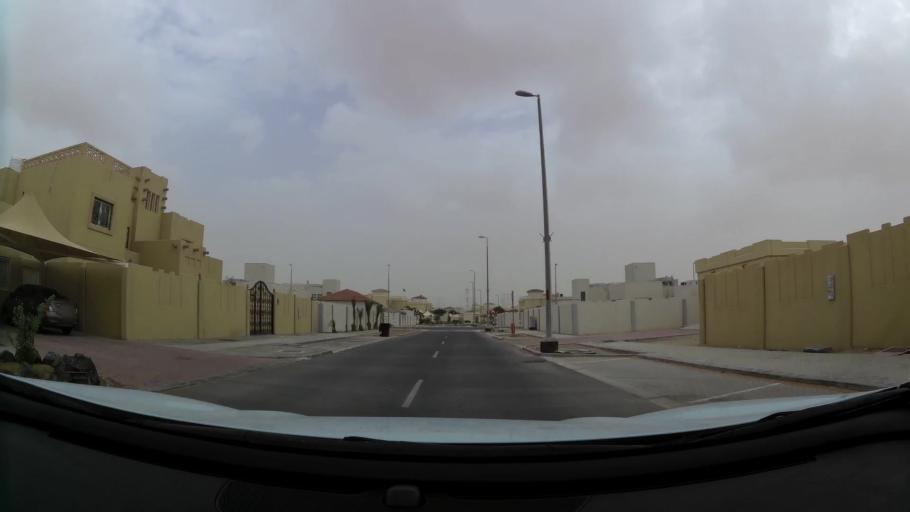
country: AE
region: Abu Dhabi
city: Abu Dhabi
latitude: 24.4554
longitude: 54.7403
